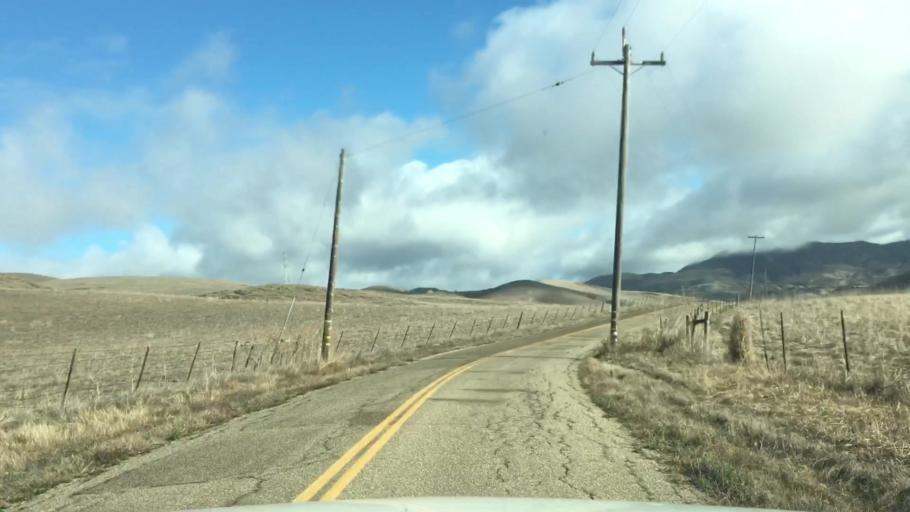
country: US
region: California
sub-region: San Luis Obispo County
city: Morro Bay
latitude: 35.3712
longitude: -120.8016
